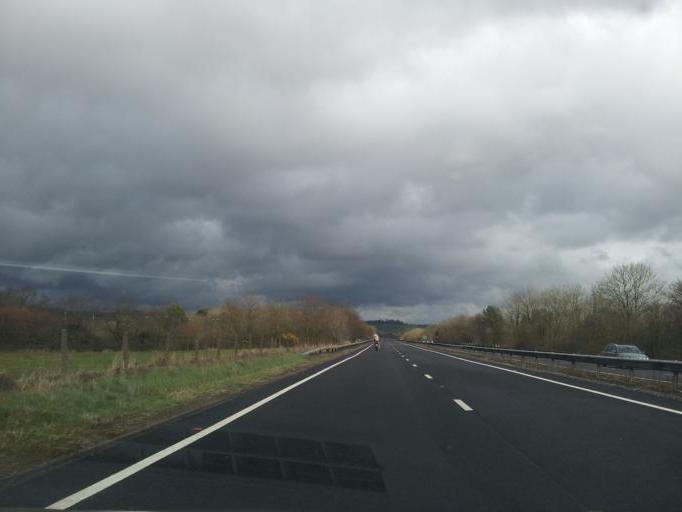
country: GB
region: England
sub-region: Somerset
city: Wincanton
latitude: 51.0462
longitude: -2.4364
